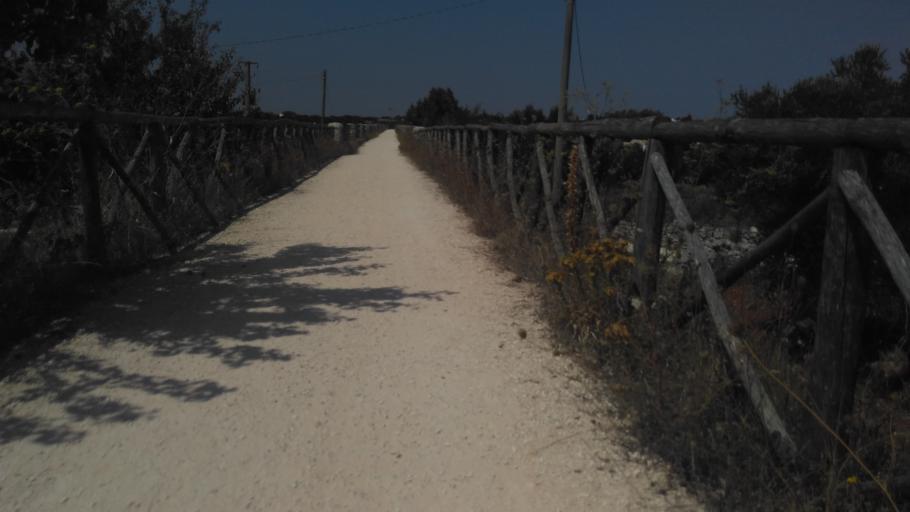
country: IT
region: Apulia
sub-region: Provincia di Brindisi
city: Cisternino
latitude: 40.6941
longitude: 17.4242
